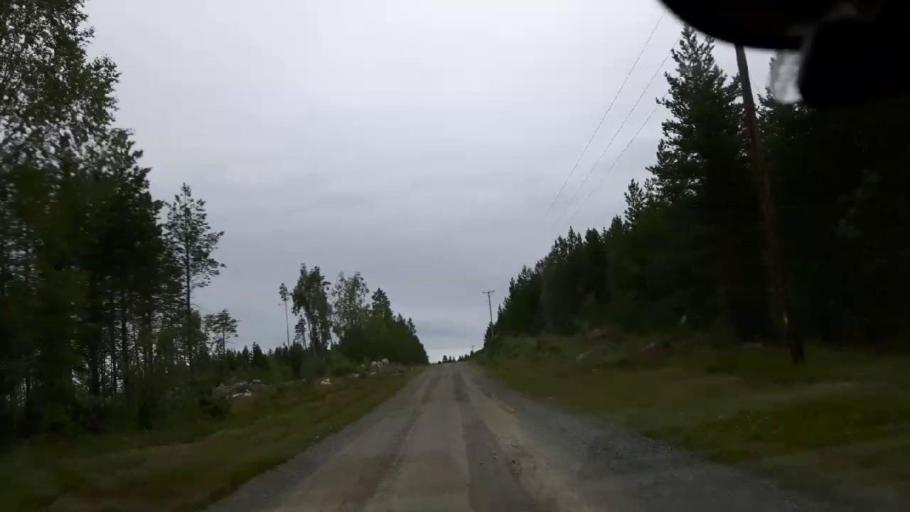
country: SE
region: Vaesternorrland
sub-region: Ange Kommun
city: Fransta
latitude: 62.8064
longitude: 16.0198
